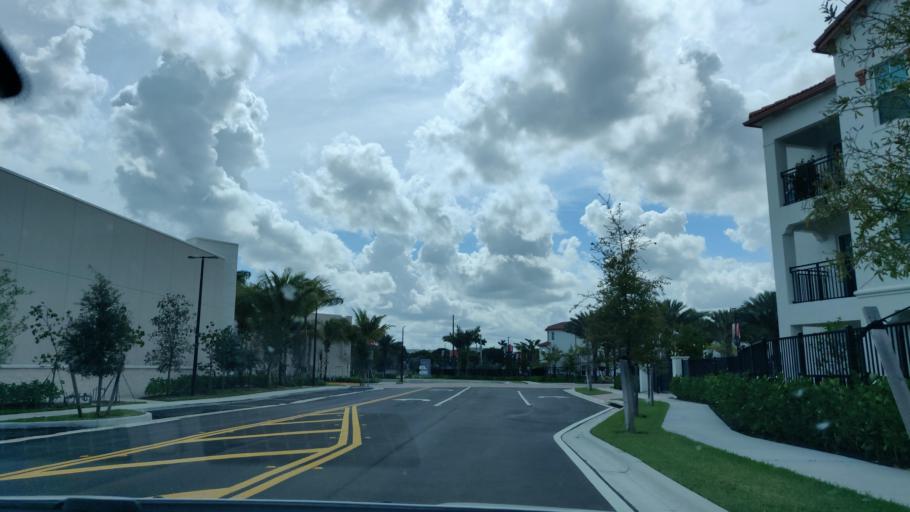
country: US
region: Florida
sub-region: Miami-Dade County
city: Country Club
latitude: 25.9798
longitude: -80.2969
